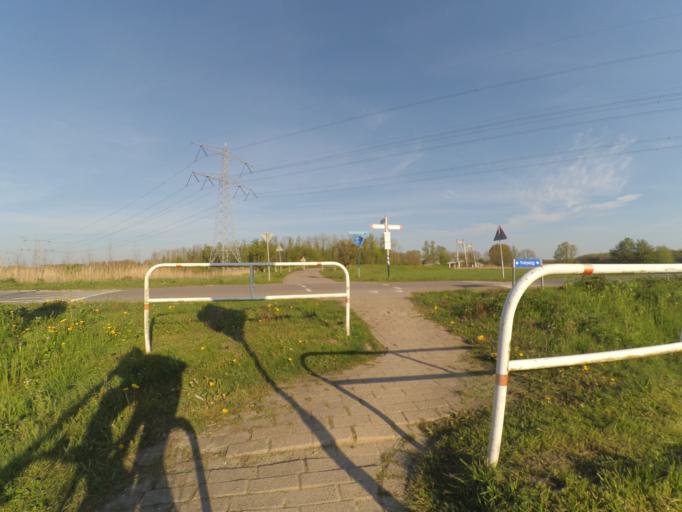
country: NL
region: Flevoland
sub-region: Gemeente Almere
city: Almere Stad
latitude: 52.3856
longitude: 5.2945
